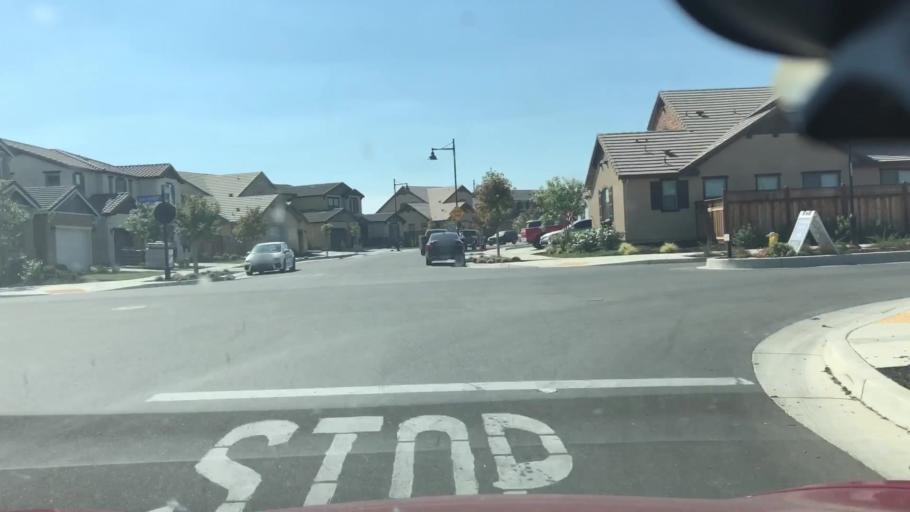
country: US
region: California
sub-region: San Joaquin County
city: Lathrop
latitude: 37.7951
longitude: -121.3278
